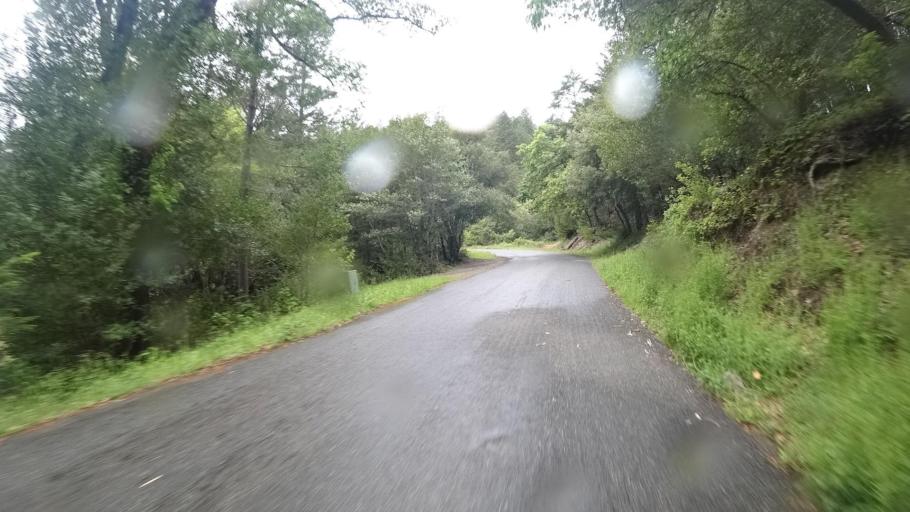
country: US
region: California
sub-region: Siskiyou County
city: Happy Camp
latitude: 41.3720
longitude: -123.5008
